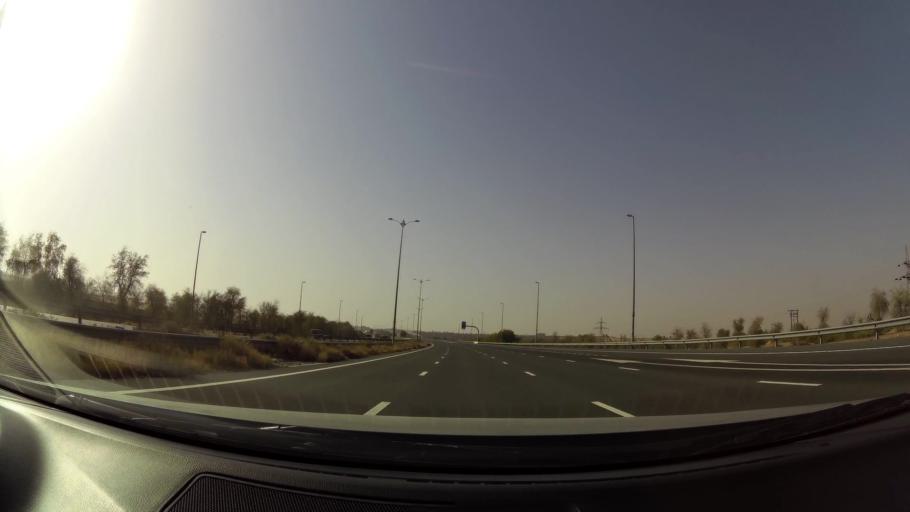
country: OM
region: Al Buraimi
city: Al Buraymi
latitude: 24.6451
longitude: 55.7060
